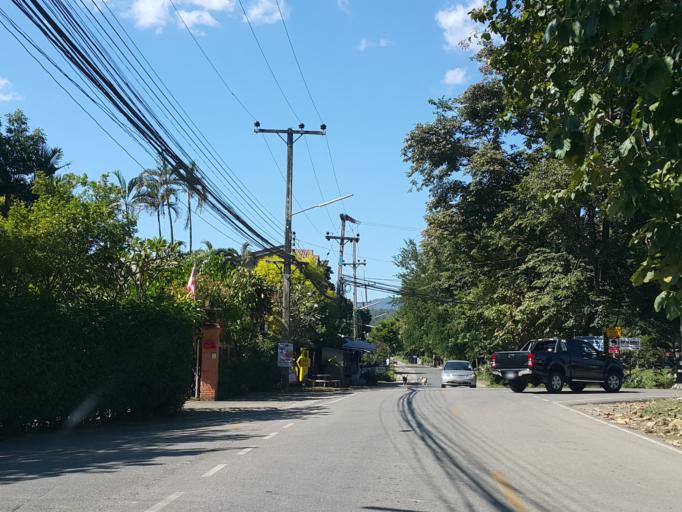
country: TH
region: Chiang Mai
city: San Sai
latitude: 18.9089
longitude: 99.1321
